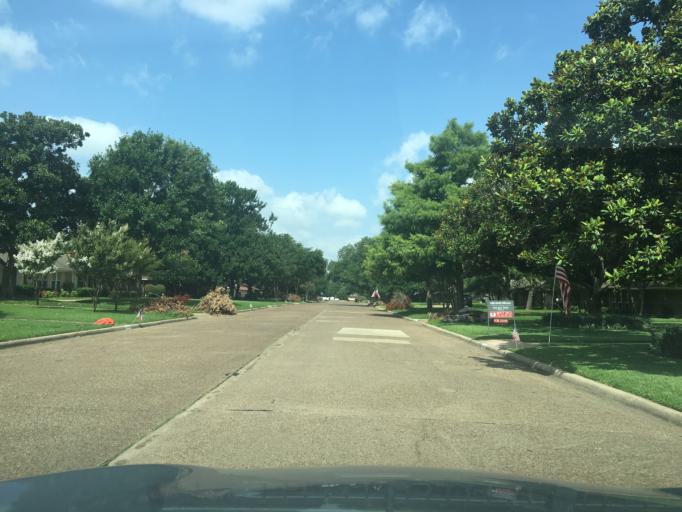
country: US
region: Texas
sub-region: Dallas County
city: Addison
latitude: 32.9143
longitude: -96.8311
